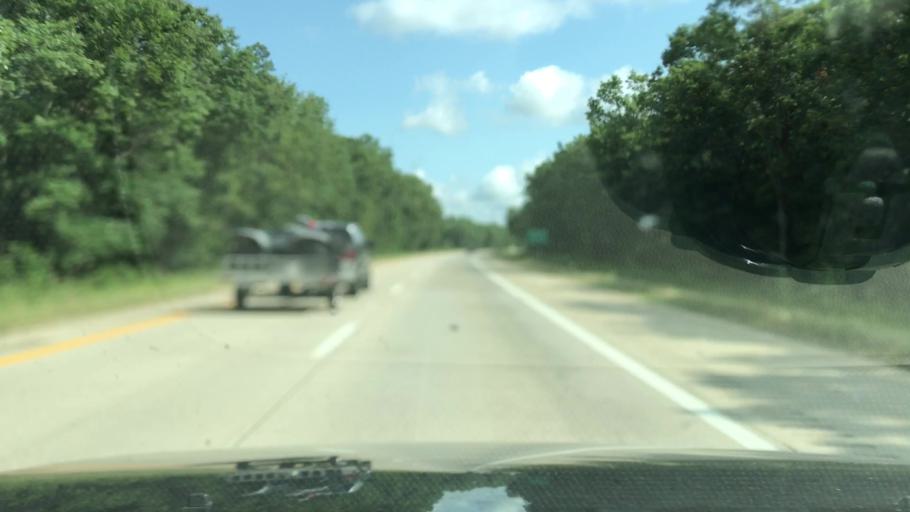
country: US
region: Michigan
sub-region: Montcalm County
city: Howard City
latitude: 43.4075
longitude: -85.5086
